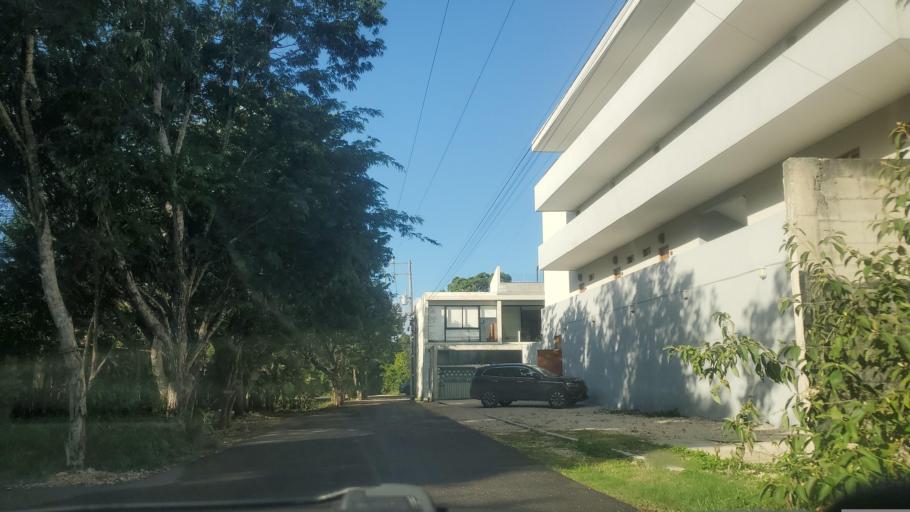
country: MX
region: Quintana Roo
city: Tulum
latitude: 20.2084
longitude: -87.4753
